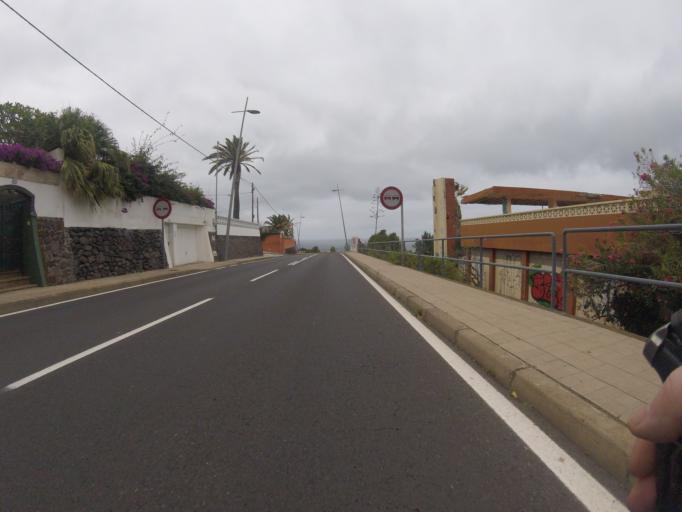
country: ES
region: Canary Islands
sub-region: Provincia de Santa Cruz de Tenerife
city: Tegueste
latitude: 28.5554
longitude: -16.3383
